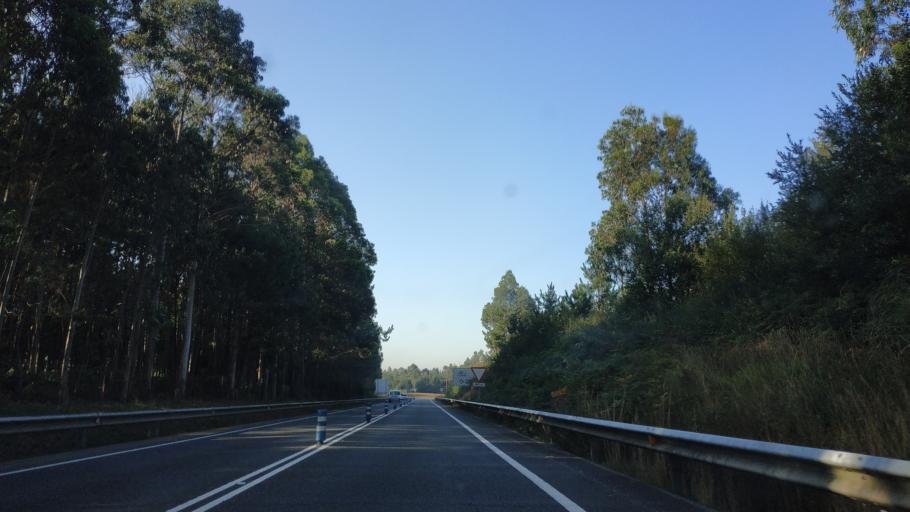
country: ES
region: Galicia
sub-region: Provincia da Coruna
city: Carballo
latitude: 43.2416
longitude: -8.6765
